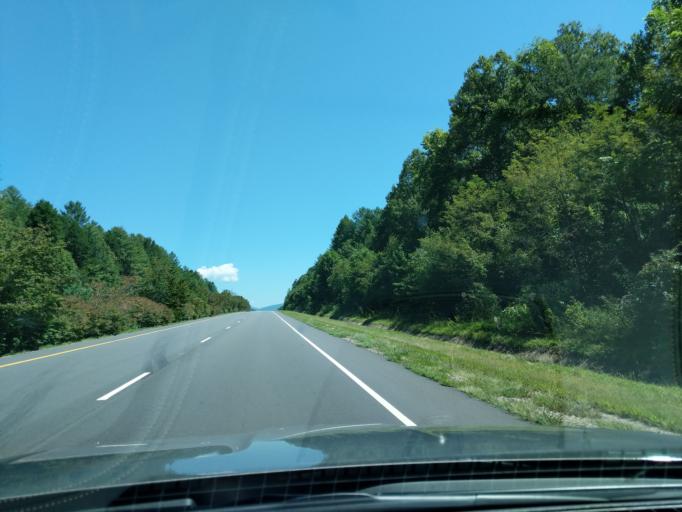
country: US
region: North Carolina
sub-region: Macon County
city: Franklin
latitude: 35.1605
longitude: -83.4483
